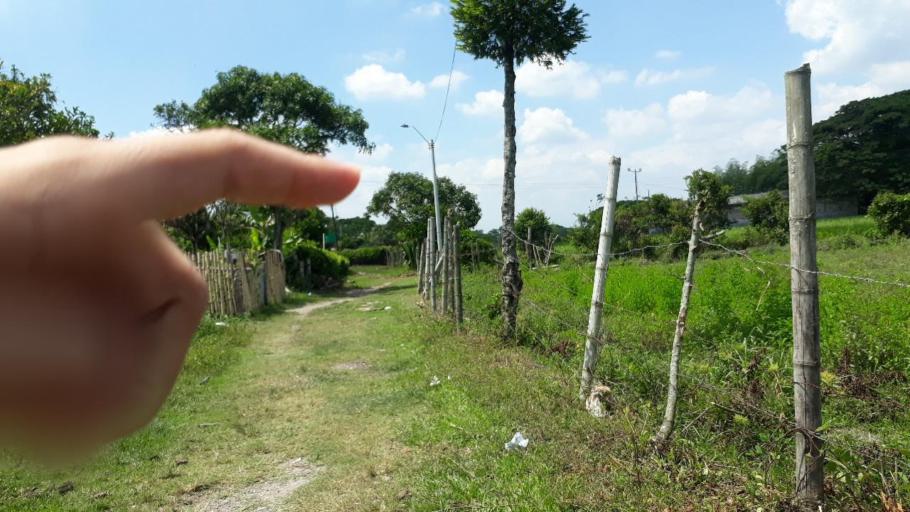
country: CO
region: Valle del Cauca
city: Jamundi
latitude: 3.1335
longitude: -76.5401
